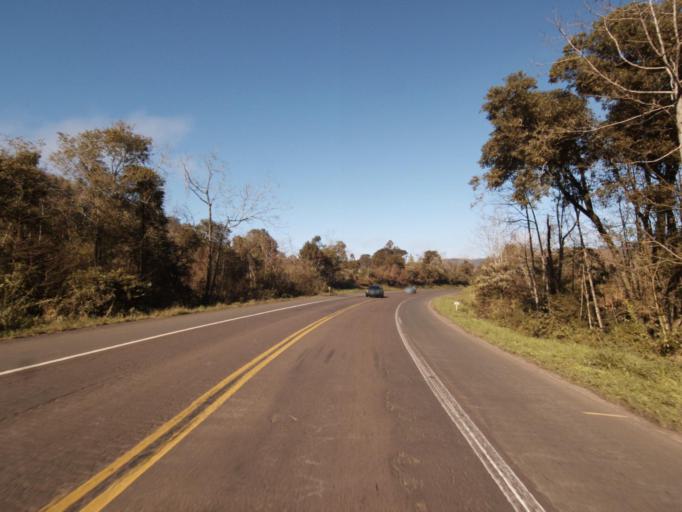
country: BR
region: Rio Grande do Sul
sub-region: Frederico Westphalen
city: Frederico Westphalen
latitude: -26.9914
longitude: -53.2257
